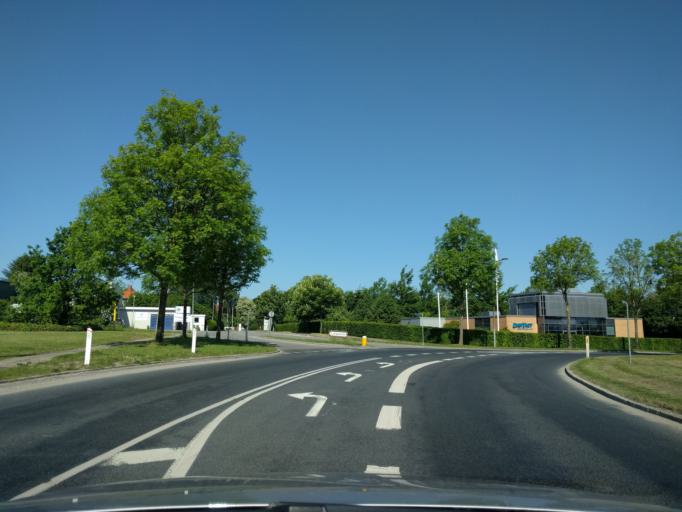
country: DK
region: South Denmark
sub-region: Odense Kommune
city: Bellinge
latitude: 55.3569
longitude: 10.3286
